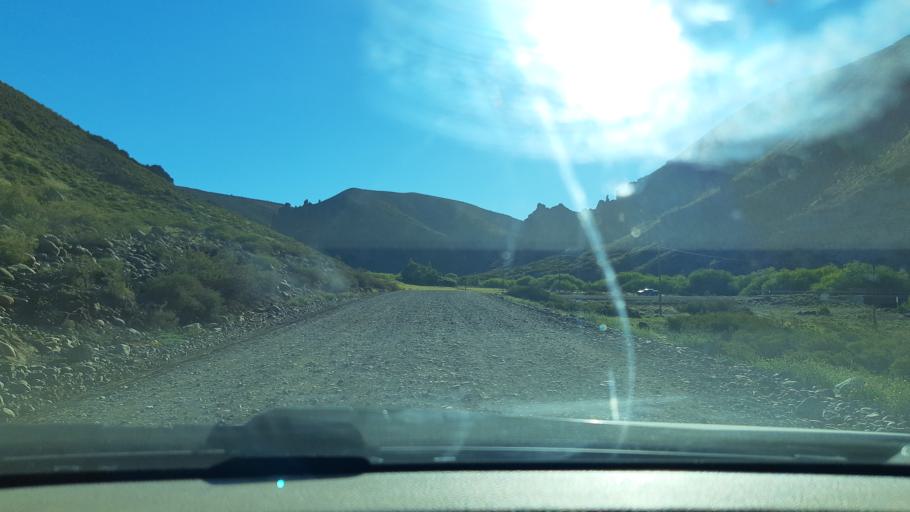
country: AR
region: Neuquen
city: Las Ovejas
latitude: -36.8020
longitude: -70.7285
